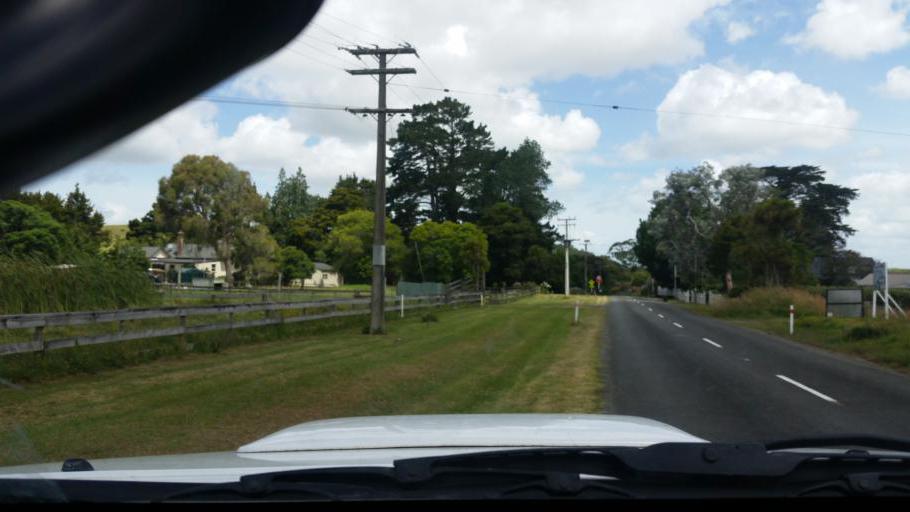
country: NZ
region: Northland
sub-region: Whangarei
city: Ruakaka
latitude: -36.0975
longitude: 174.2319
